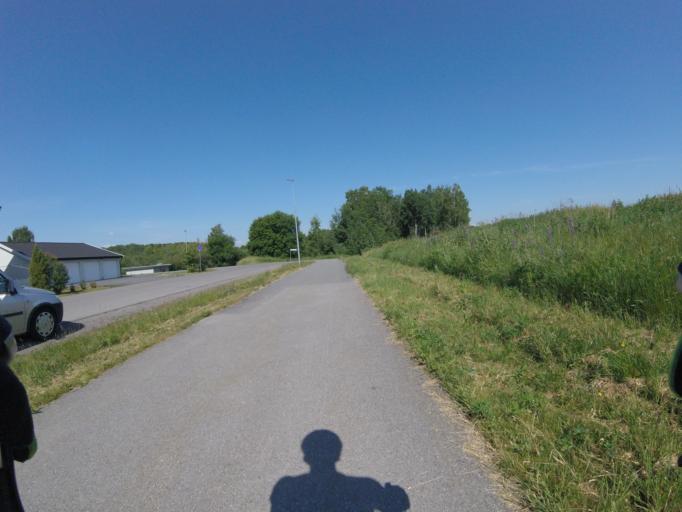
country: NO
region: Akershus
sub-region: Skedsmo
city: Lillestrom
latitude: 59.9662
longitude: 11.0363
